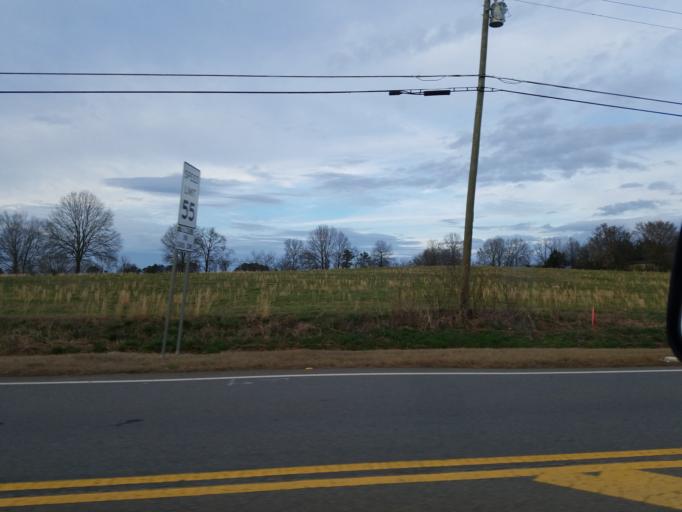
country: US
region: Georgia
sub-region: Bartow County
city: Adairsville
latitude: 34.4483
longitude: -84.8338
